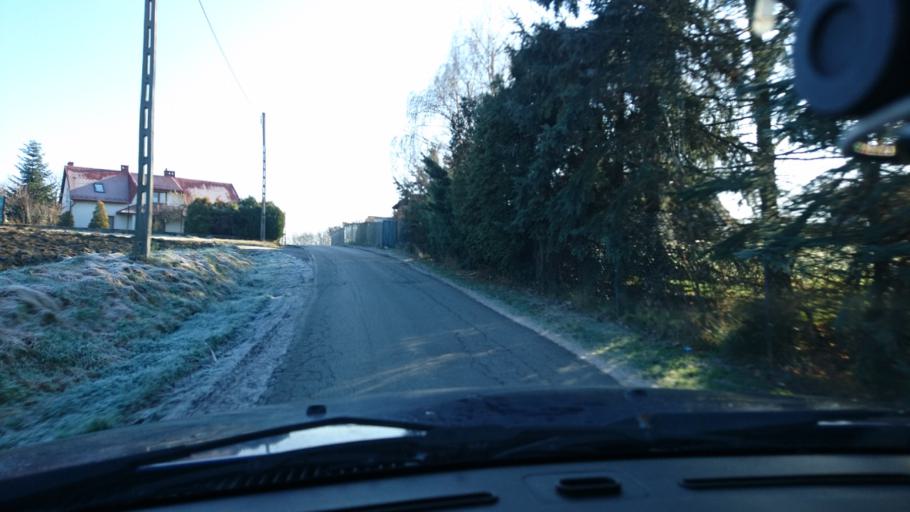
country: PL
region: Silesian Voivodeship
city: Janowice
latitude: 49.8926
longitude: 19.1139
